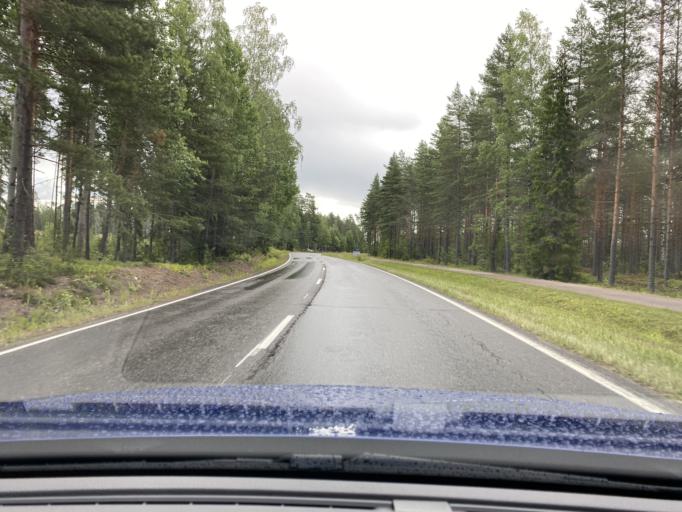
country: FI
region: Uusimaa
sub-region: Helsinki
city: Hyvinge
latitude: 60.5748
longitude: 24.7752
